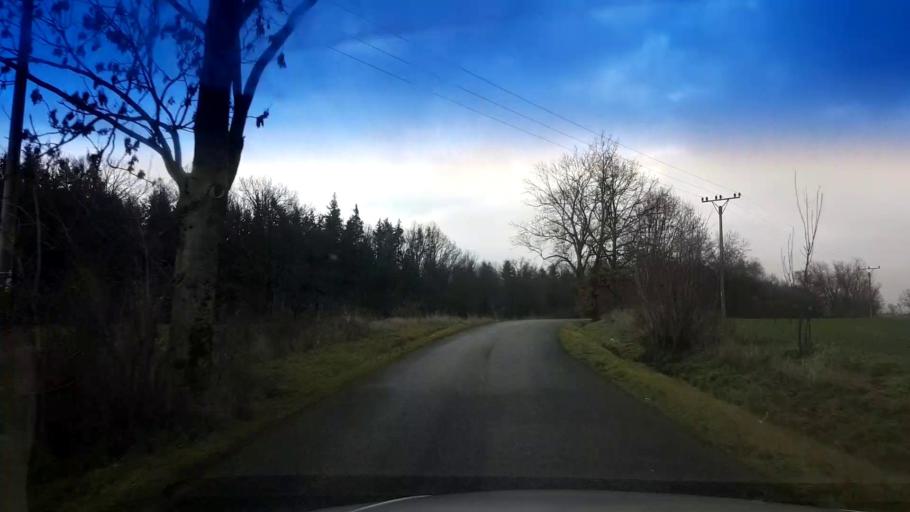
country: CZ
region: Karlovarsky
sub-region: Okres Cheb
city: Cheb
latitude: 50.0492
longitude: 12.3713
